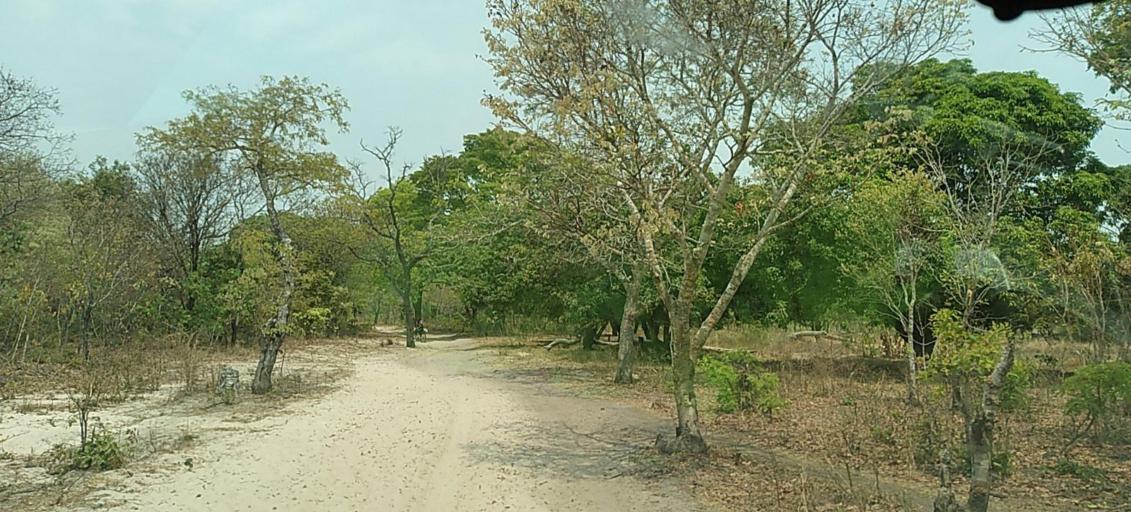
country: ZM
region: North-Western
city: Kabompo
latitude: -13.5387
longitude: 24.4539
